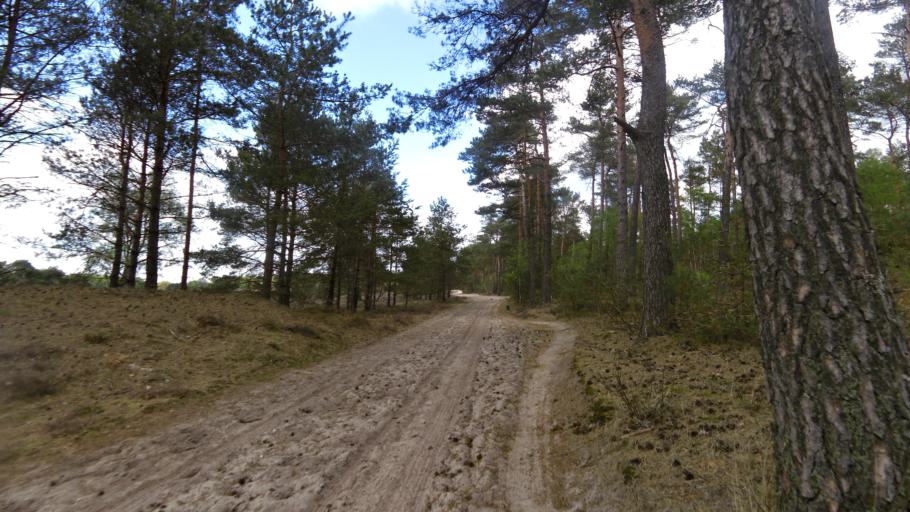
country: NL
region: Gelderland
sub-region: Gemeente Apeldoorn
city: Loenen
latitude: 52.0785
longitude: 6.0108
